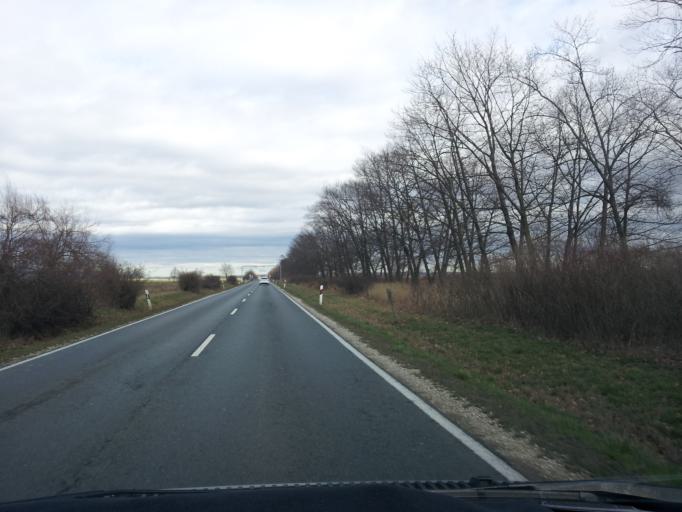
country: HU
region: Vas
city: Gencsapati
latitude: 47.2868
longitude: 16.6109
